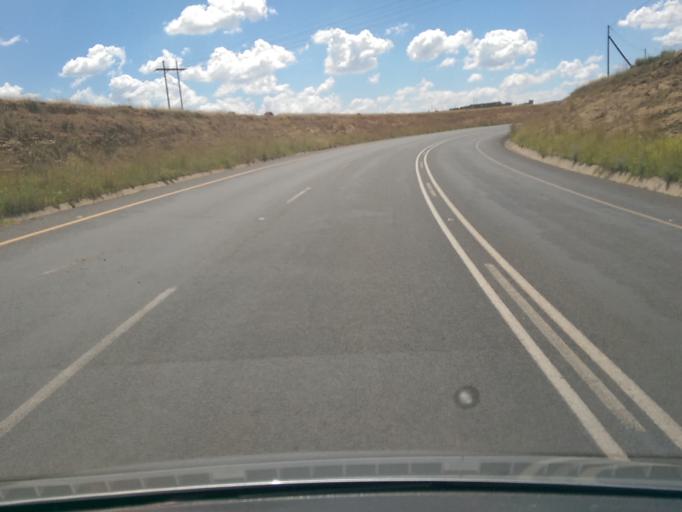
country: LS
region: Maseru
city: Maseru
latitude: -29.3749
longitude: 27.4763
